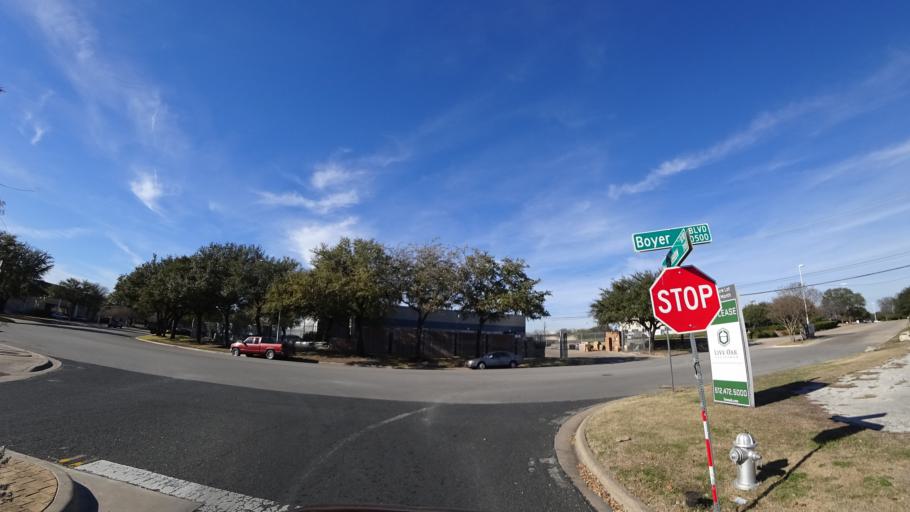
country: US
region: Texas
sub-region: Travis County
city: Wells Branch
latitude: 30.3832
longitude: -97.7112
